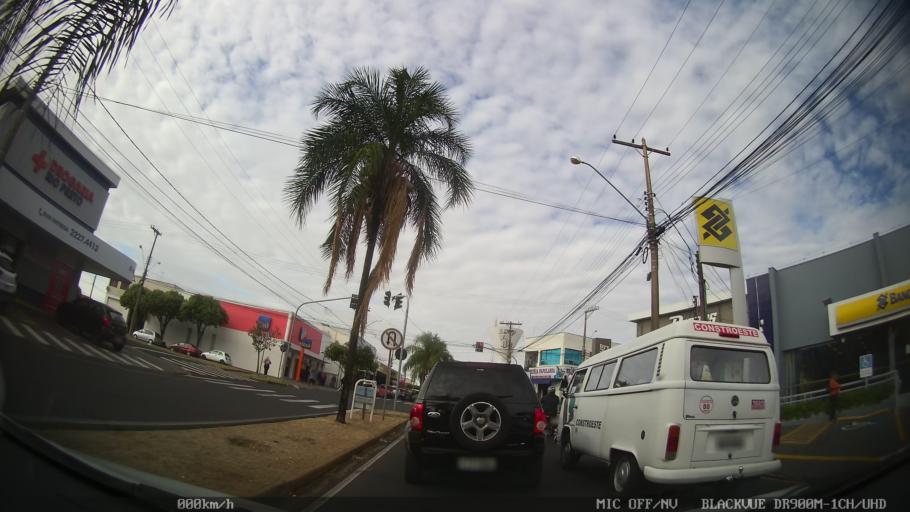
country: BR
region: Sao Paulo
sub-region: Sao Jose Do Rio Preto
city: Sao Jose do Rio Preto
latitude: -20.8281
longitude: -49.3731
